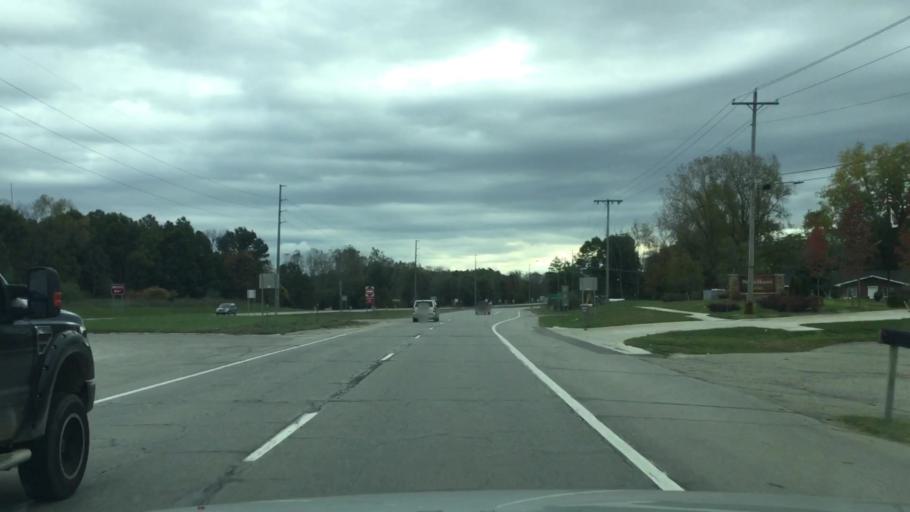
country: US
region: Michigan
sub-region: Livingston County
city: Brighton
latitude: 42.6362
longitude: -83.7265
